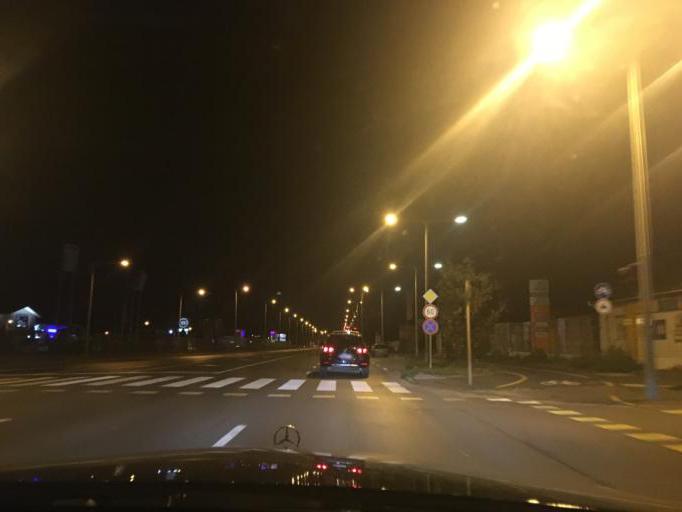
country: HU
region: Hajdu-Bihar
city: Debrecen
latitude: 47.4997
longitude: 21.6313
